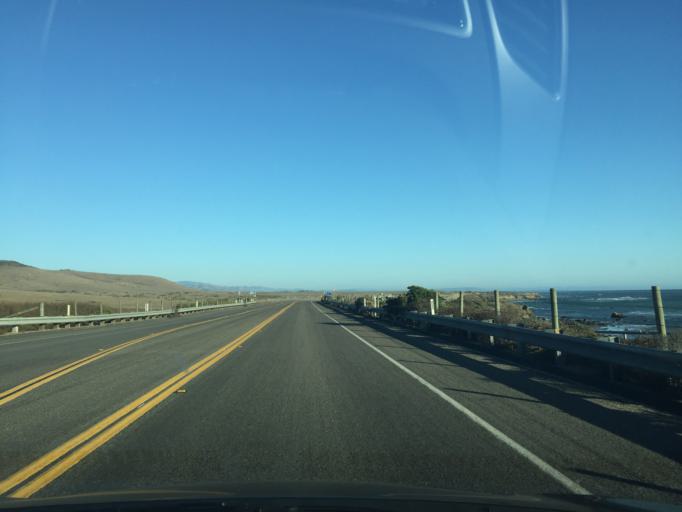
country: US
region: California
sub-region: San Luis Obispo County
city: Cambria
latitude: 35.6644
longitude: -121.2600
